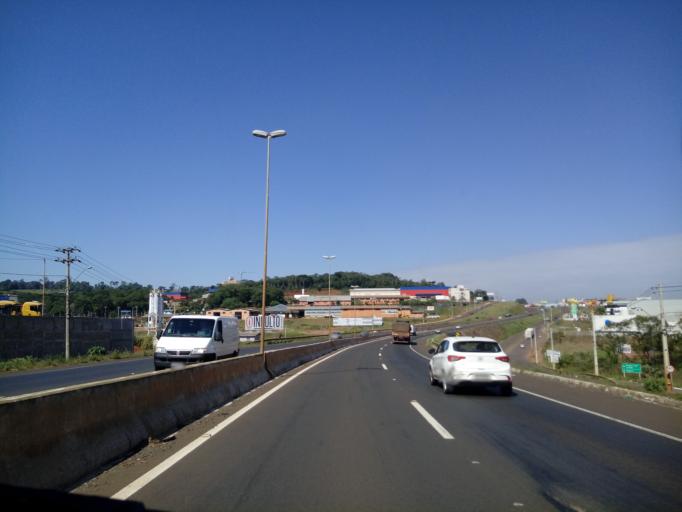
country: BR
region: Santa Catarina
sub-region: Chapeco
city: Chapeco
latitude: -27.0489
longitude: -52.6353
